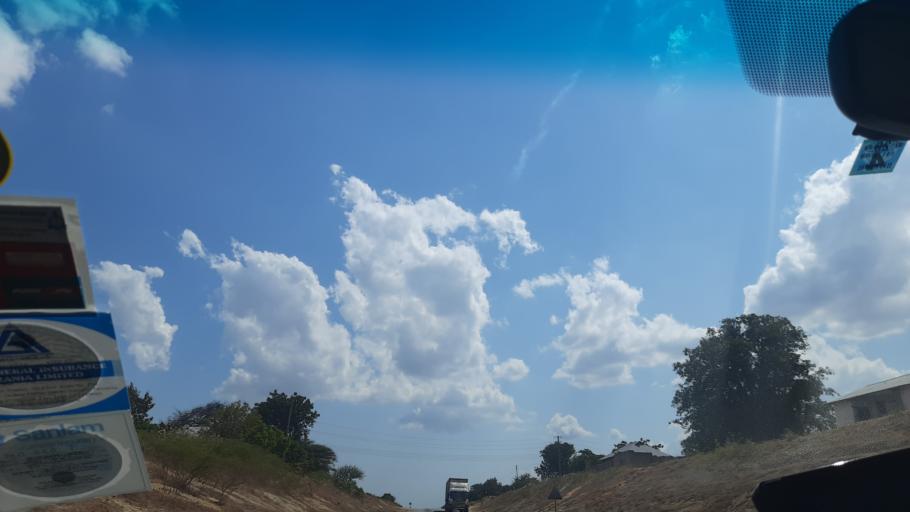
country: TZ
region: Singida
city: Kintinku
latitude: -6.0142
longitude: 35.4365
